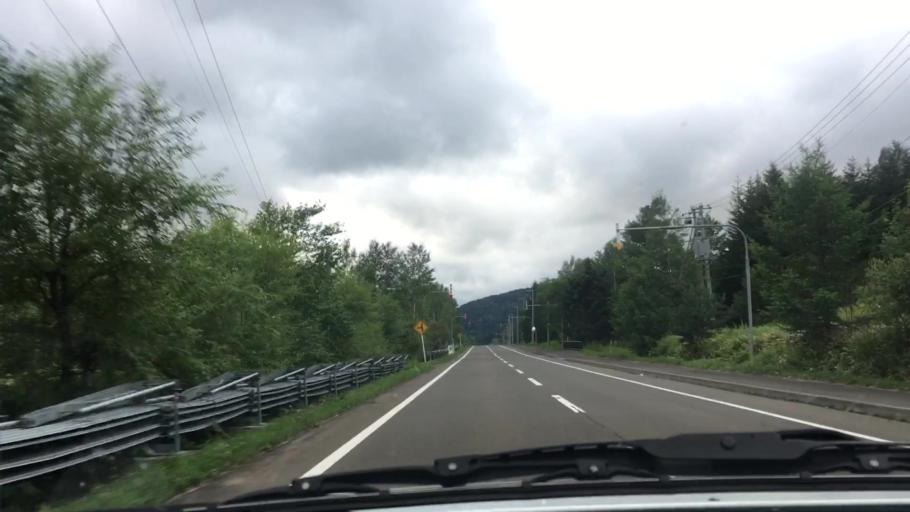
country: JP
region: Hokkaido
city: Shimo-furano
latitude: 43.0548
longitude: 142.6338
